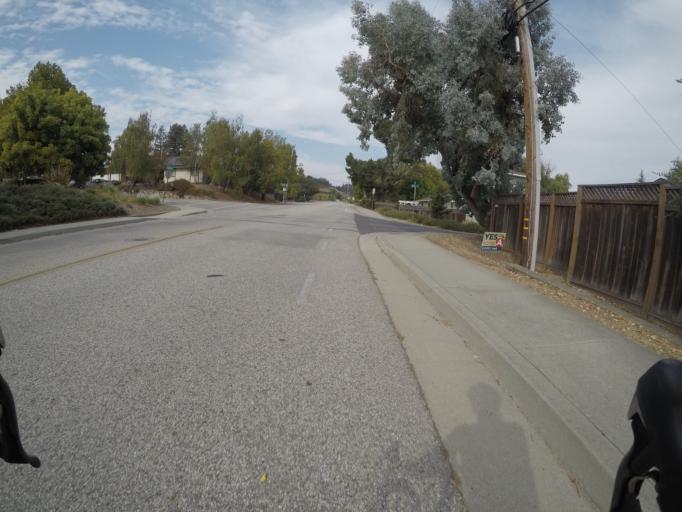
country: US
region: California
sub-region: Santa Cruz County
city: Scotts Valley
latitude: 37.0675
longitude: -122.0054
